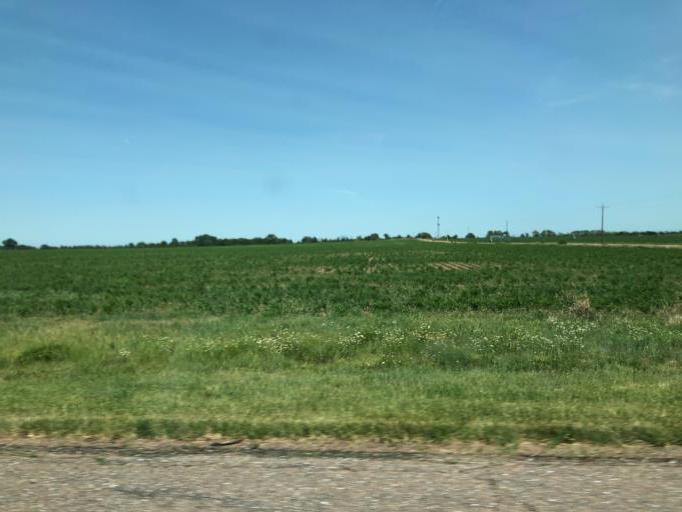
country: US
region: Nebraska
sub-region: Thayer County
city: Hebron
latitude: 40.2780
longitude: -97.5765
